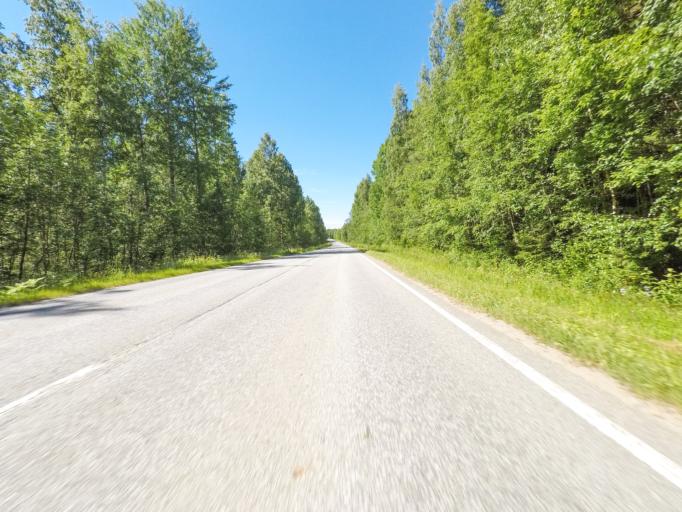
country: FI
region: Southern Savonia
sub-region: Savonlinna
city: Rantasalmi
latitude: 62.0067
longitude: 28.4189
